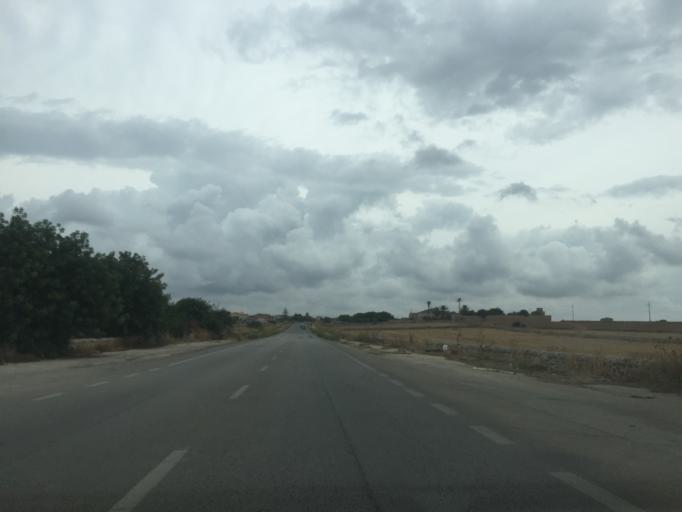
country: IT
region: Sicily
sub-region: Ragusa
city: Marina di Ragusa
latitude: 36.8065
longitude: 14.5632
